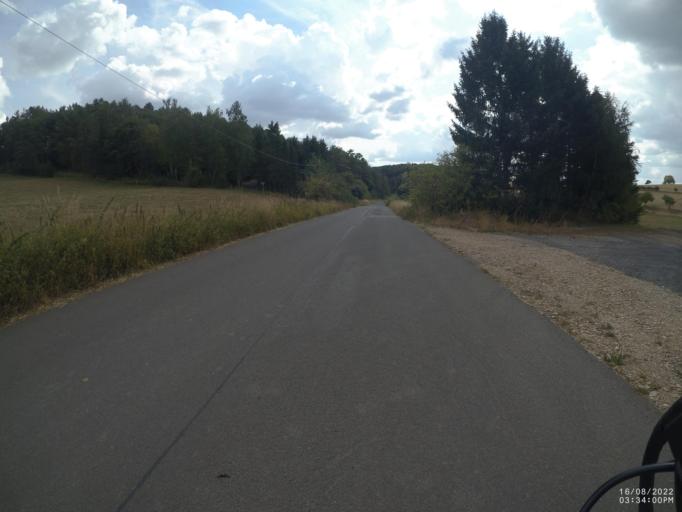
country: DE
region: Rheinland-Pfalz
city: Berndorf
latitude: 50.3027
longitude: 6.6969
